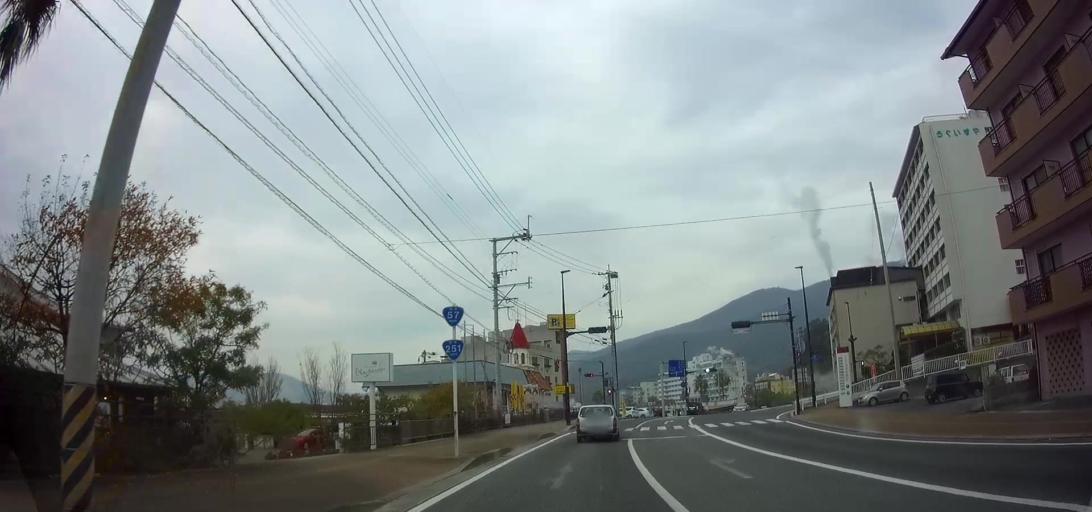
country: JP
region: Nagasaki
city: Shimabara
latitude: 32.7251
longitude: 130.2043
